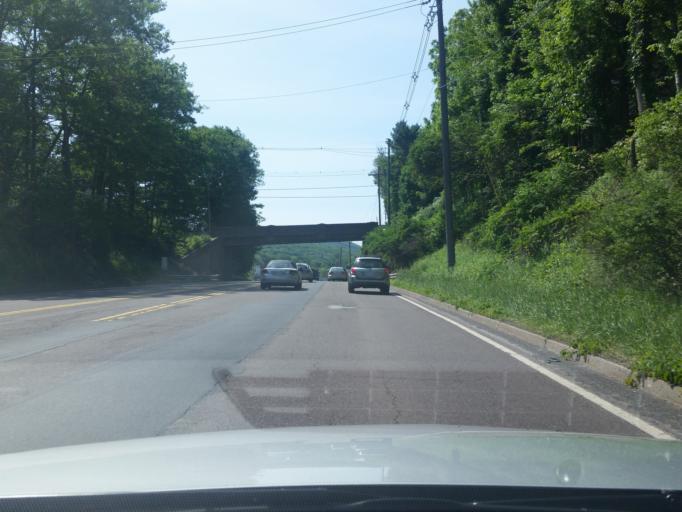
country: US
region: Pennsylvania
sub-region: Luzerne County
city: Shavertown
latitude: 41.3265
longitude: -75.9460
